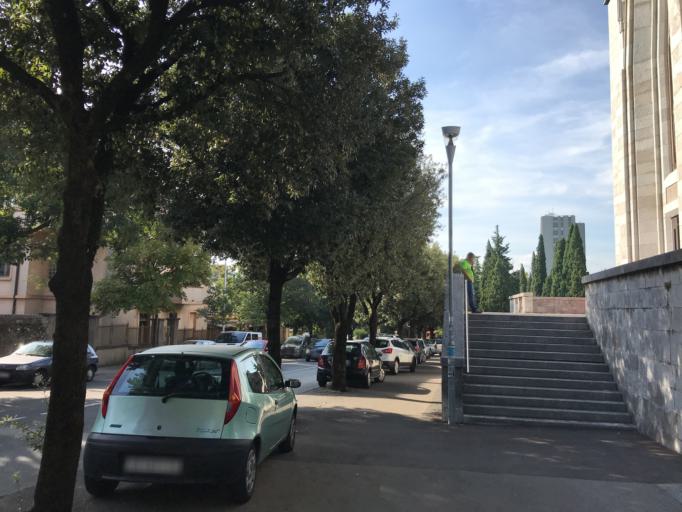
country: HR
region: Primorsko-Goranska
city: Drenova
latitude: 45.3325
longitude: 14.4441
